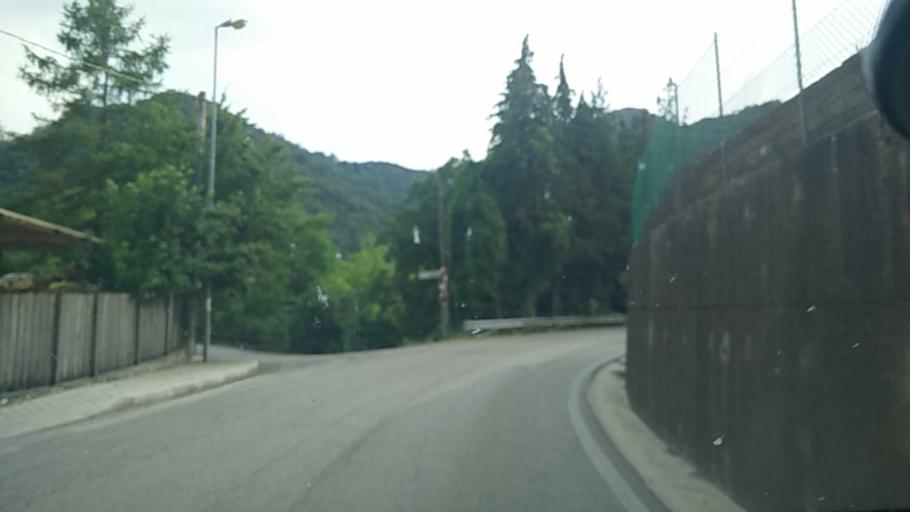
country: IT
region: Veneto
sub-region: Provincia di Treviso
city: Follina
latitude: 45.9323
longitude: 12.1280
